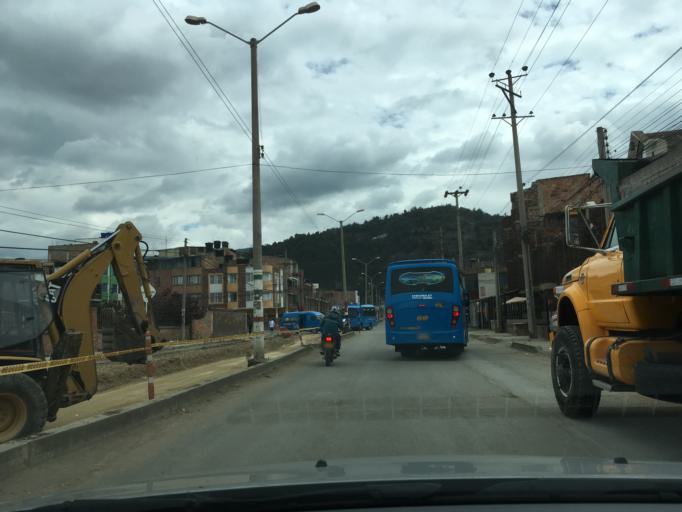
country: CO
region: Boyaca
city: Sogamoso
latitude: 5.7035
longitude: -72.9413
